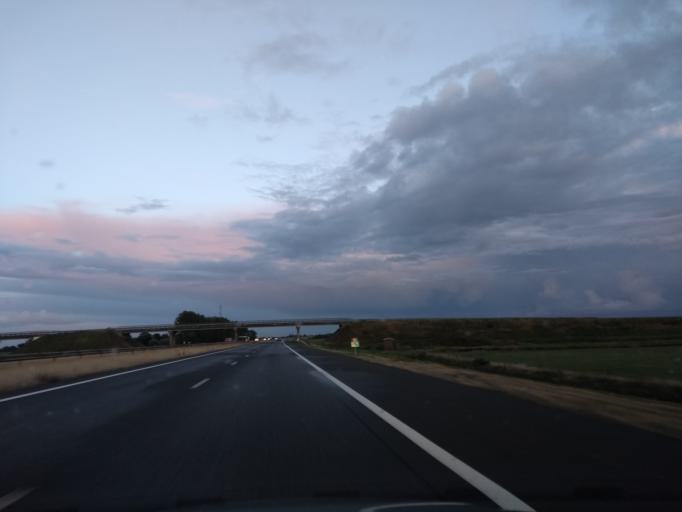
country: NL
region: Friesland
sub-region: Sudwest Fryslan
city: Oppenhuizen
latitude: 52.9874
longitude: 5.7255
